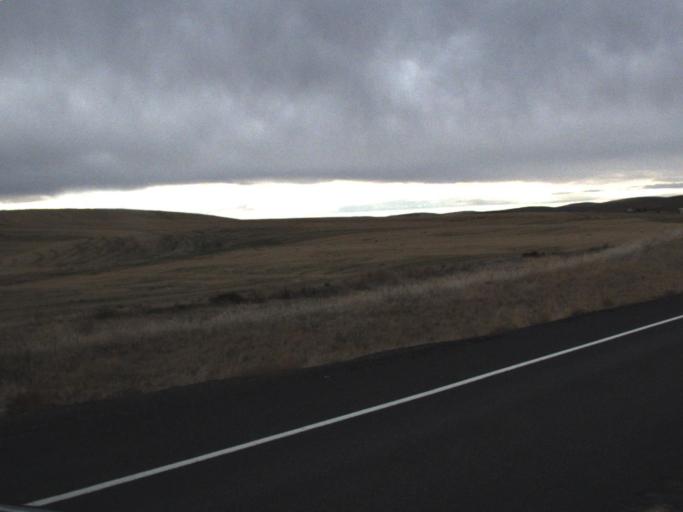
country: US
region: Washington
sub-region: Garfield County
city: Pomeroy
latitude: 46.8085
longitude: -117.8257
